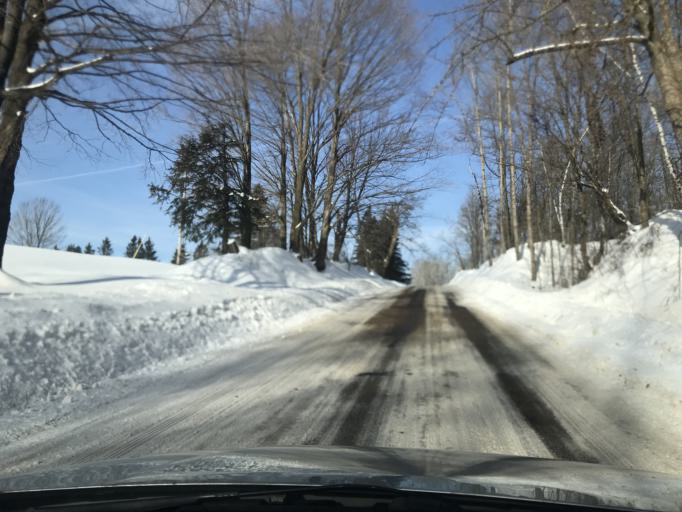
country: US
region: Wisconsin
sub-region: Menominee County
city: Legend Lake
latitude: 45.2997
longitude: -88.4917
